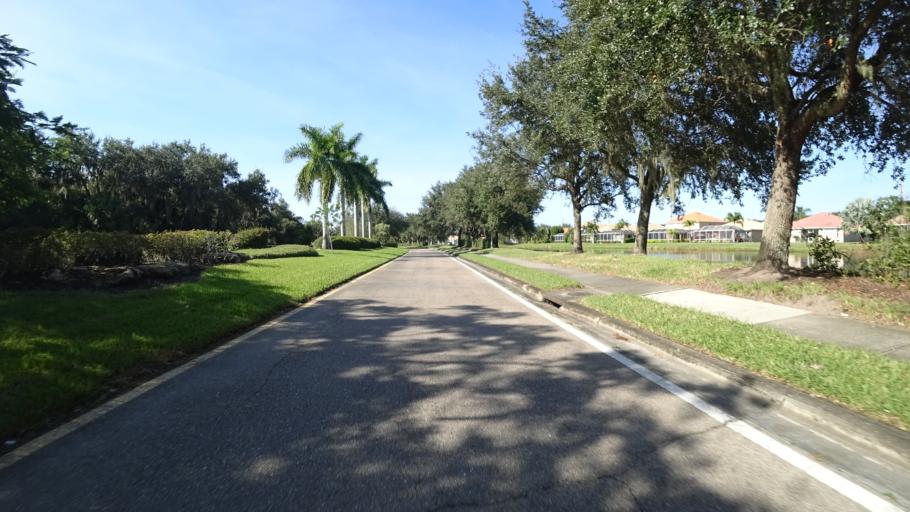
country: US
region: Florida
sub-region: Sarasota County
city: Desoto Lakes
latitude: 27.4169
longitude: -82.4639
